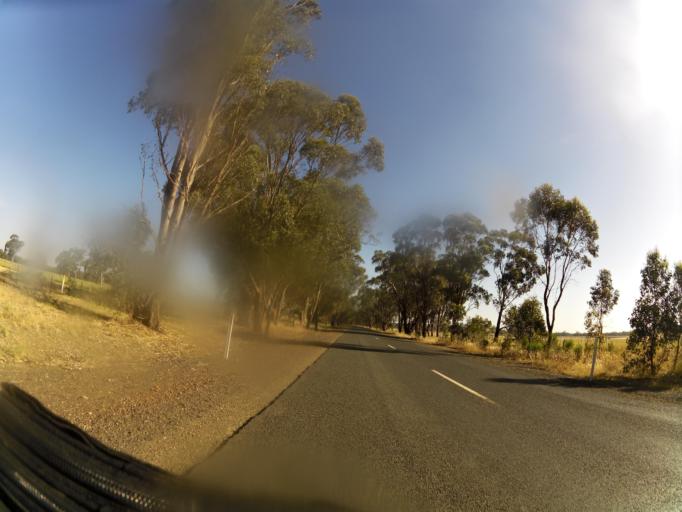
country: AU
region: Victoria
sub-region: Murrindindi
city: Kinglake West
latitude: -36.9749
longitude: 145.1099
